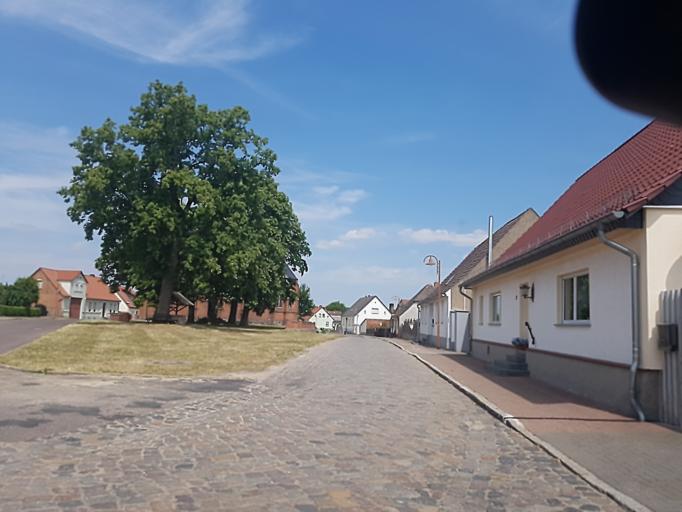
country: DE
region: Brandenburg
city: Gorzke
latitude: 52.0708
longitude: 12.3077
